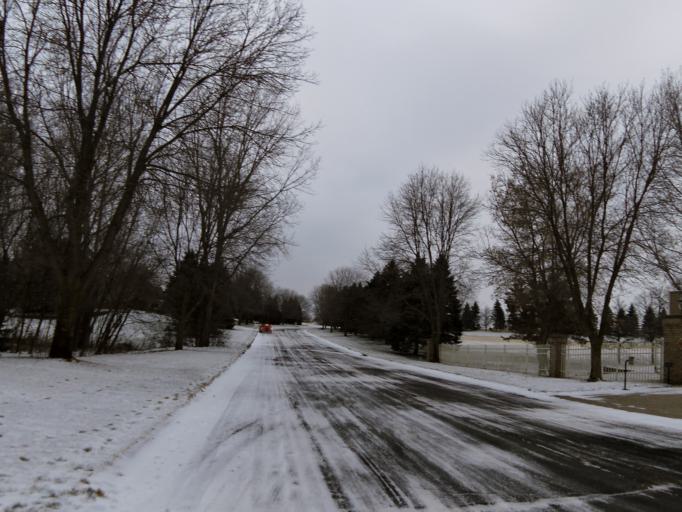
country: US
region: Minnesota
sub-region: Washington County
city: Lakeland
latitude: 44.9593
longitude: -92.8254
